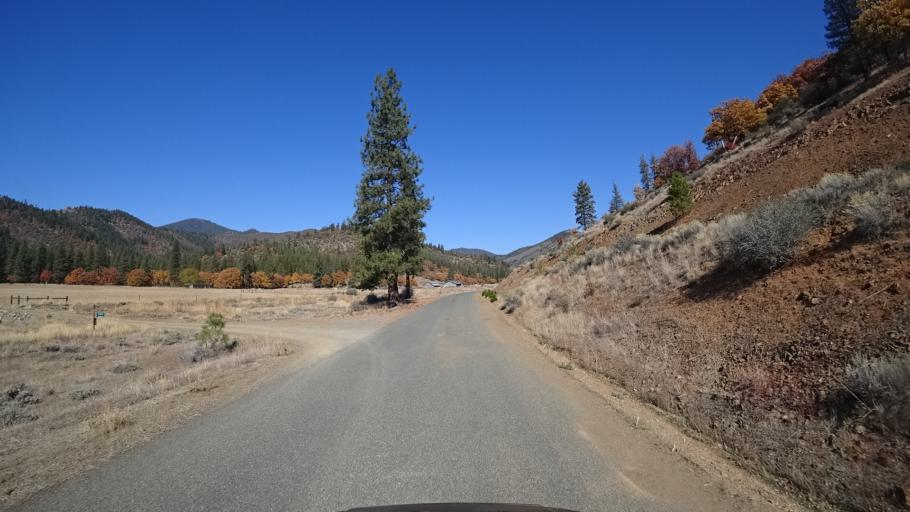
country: US
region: California
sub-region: Siskiyou County
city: Yreka
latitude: 41.6422
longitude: -122.8886
